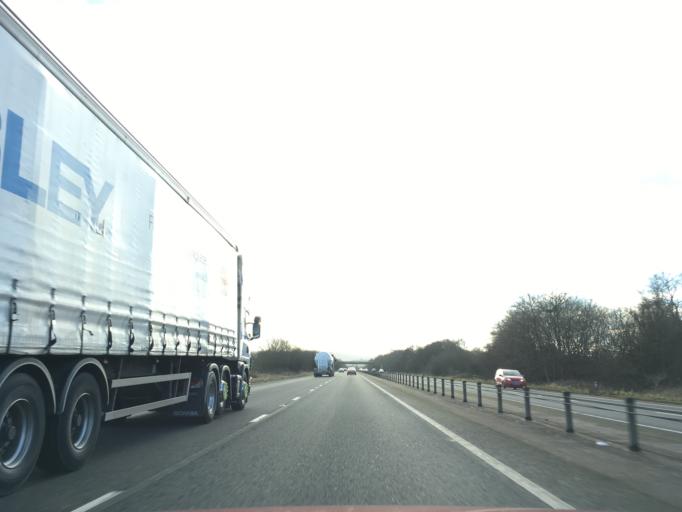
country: GB
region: Wales
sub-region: Monmouthshire
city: Llangwm
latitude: 51.7486
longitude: -2.8420
